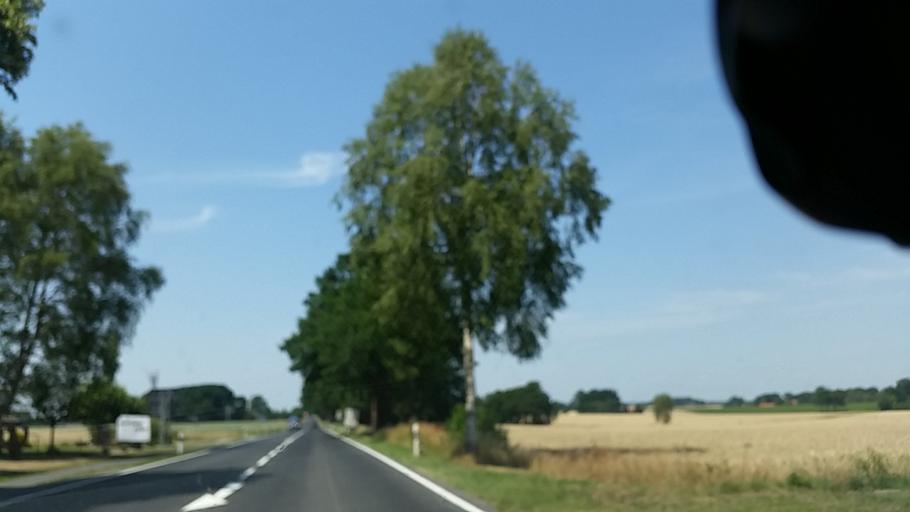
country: DE
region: Lower Saxony
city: Wietzen
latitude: 52.7284
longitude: 9.0422
